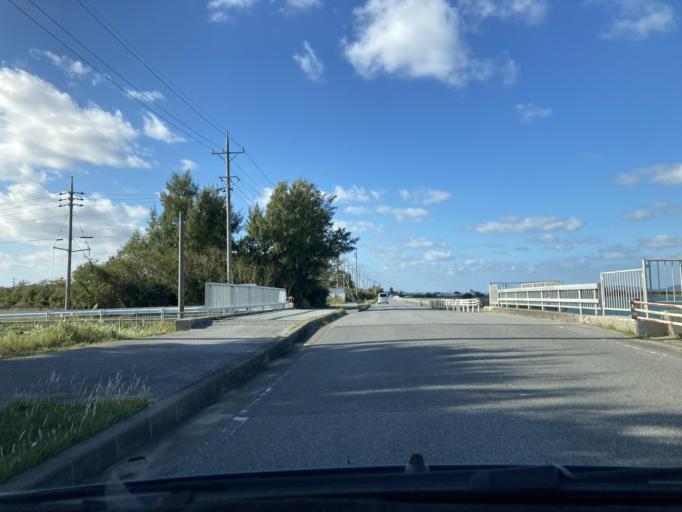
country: JP
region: Okinawa
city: Katsuren-haebaru
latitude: 26.3264
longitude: 127.9114
